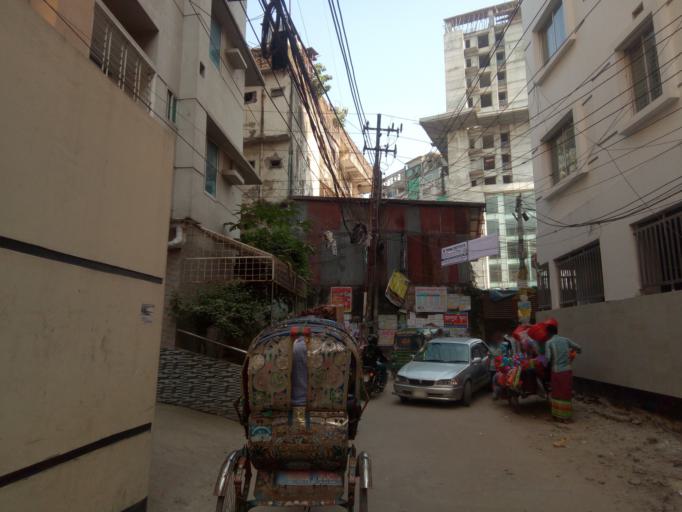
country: BD
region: Dhaka
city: Paltan
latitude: 23.7542
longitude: 90.4145
